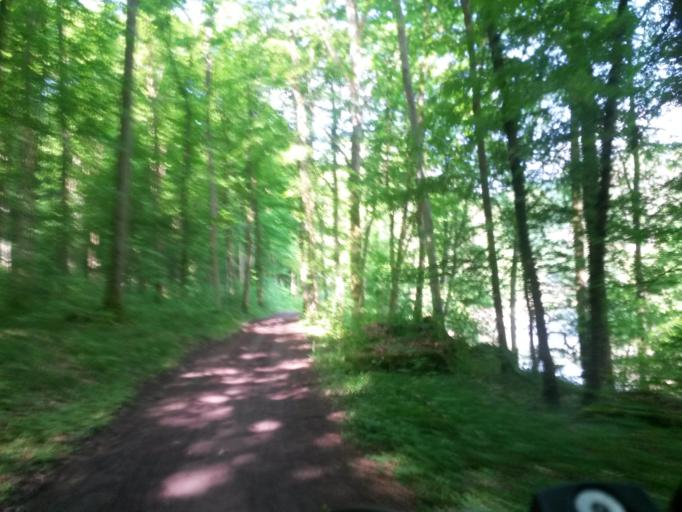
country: DE
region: Bavaria
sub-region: Regierungsbezirk Unterfranken
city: Ramsthal
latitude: 50.1669
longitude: 10.0601
